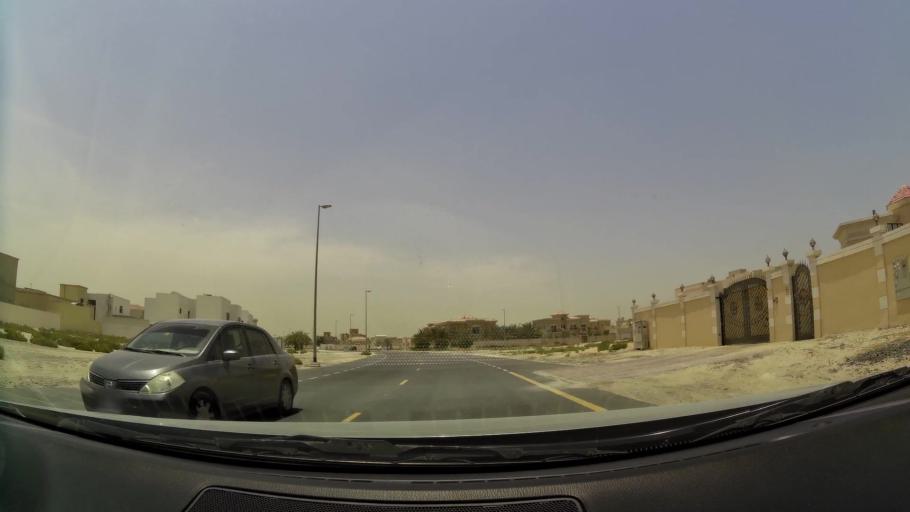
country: AE
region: Dubai
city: Dubai
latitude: 25.0885
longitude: 55.2258
